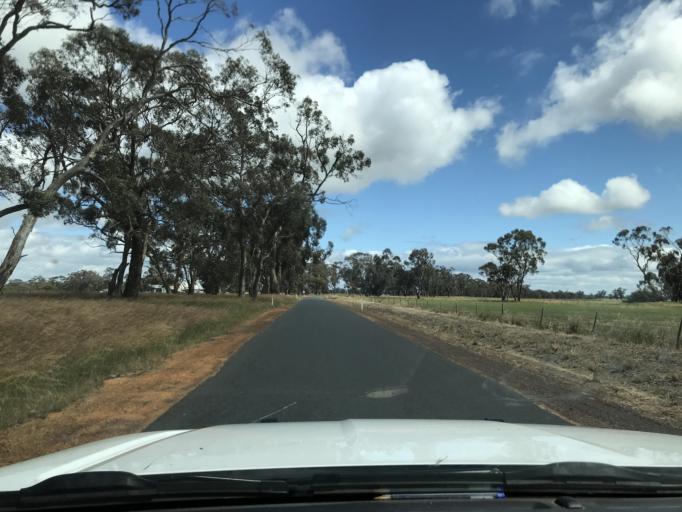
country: AU
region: Victoria
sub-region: Horsham
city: Horsham
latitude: -36.8075
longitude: 141.4800
